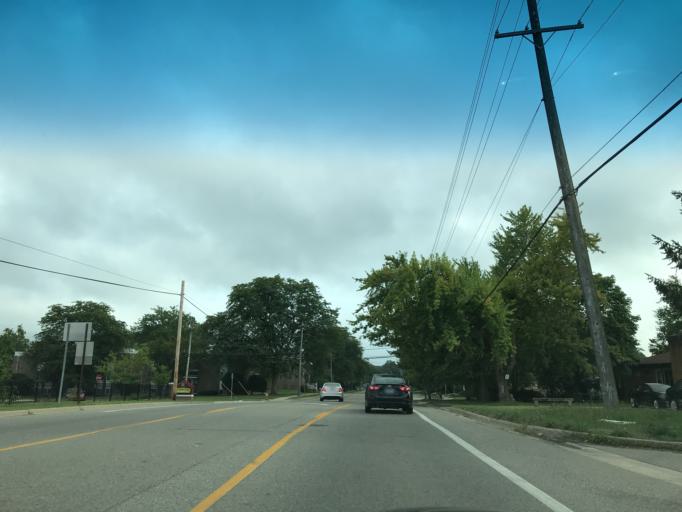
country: US
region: Michigan
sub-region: Washtenaw County
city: Ypsilanti
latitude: 42.2496
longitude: -83.6611
